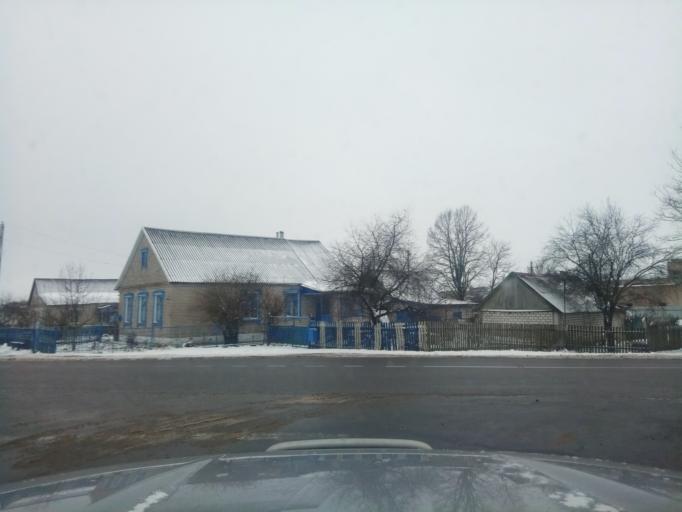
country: BY
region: Minsk
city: Kapyl'
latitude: 53.1617
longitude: 27.0859
